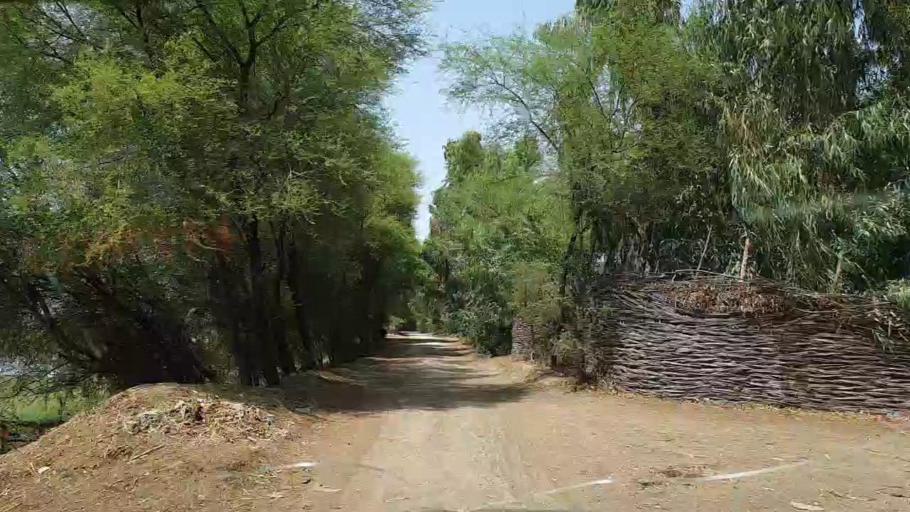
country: PK
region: Sindh
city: Ghotki
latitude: 28.0874
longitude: 69.3109
